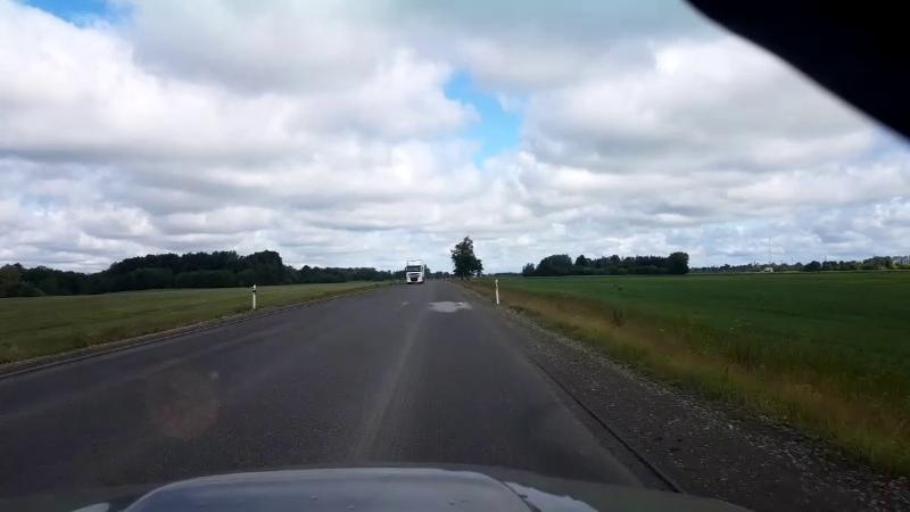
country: LV
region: Bauskas Rajons
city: Bauska
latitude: 56.2942
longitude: 24.3488
